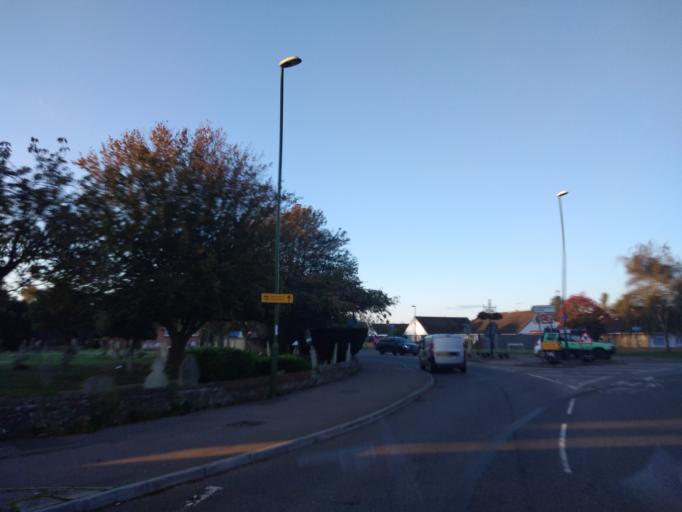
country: GB
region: England
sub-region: West Sussex
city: Littlehampton
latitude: 50.8199
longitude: -0.5281
